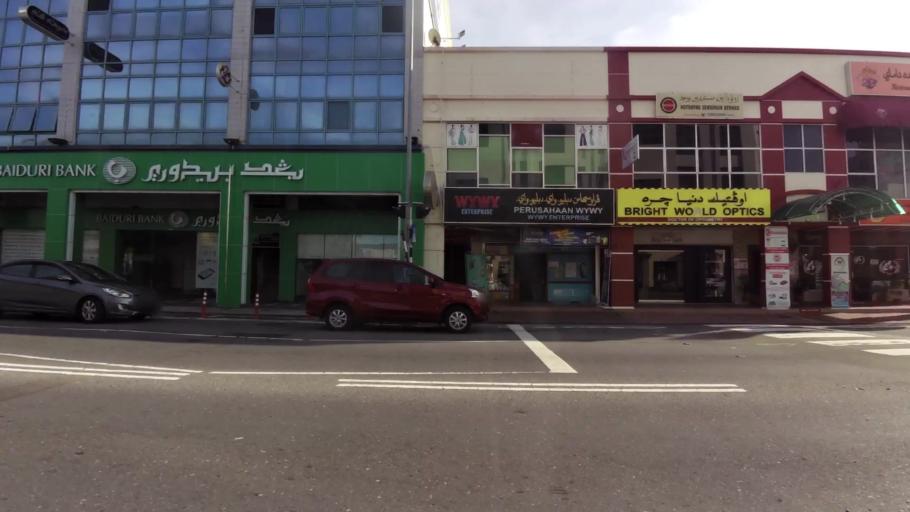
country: BN
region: Belait
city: Kuala Belait
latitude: 4.5816
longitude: 114.1917
